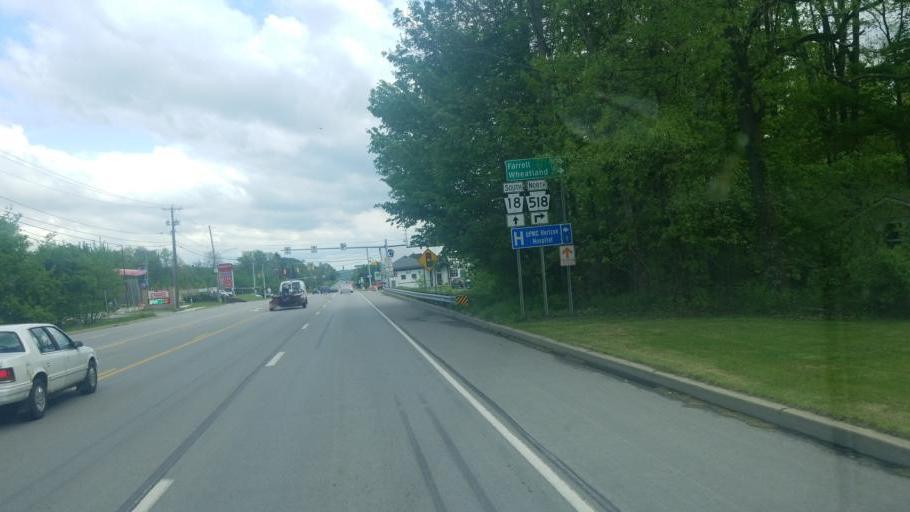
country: US
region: Pennsylvania
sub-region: Mercer County
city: Hermitage
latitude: 41.2030
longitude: -80.4567
